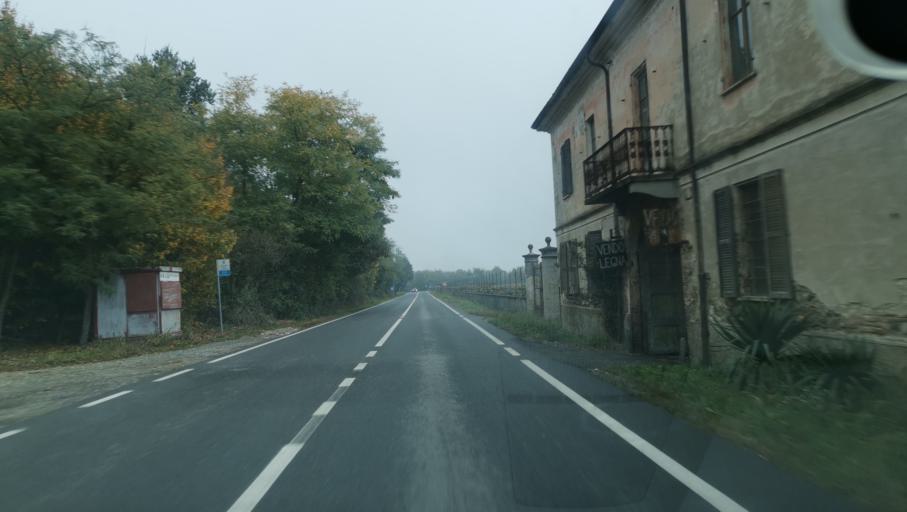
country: IT
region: Piedmont
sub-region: Provincia di Vercelli
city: Alice Castello
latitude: 45.3818
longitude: 8.0832
